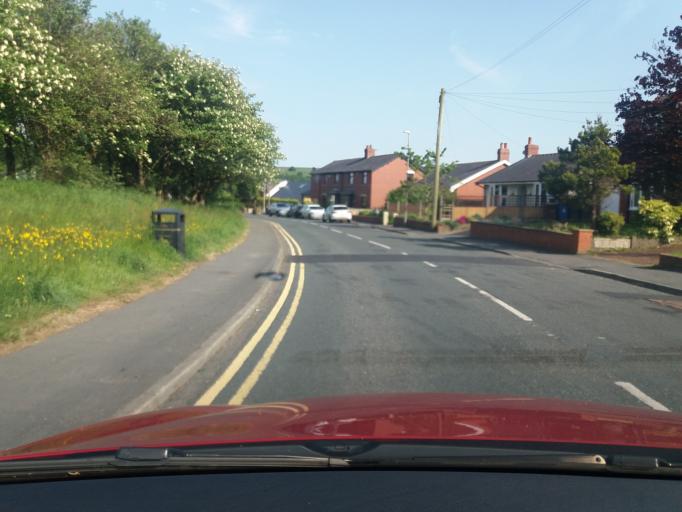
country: GB
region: England
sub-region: Lancashire
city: Chorley
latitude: 53.6891
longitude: -2.5736
